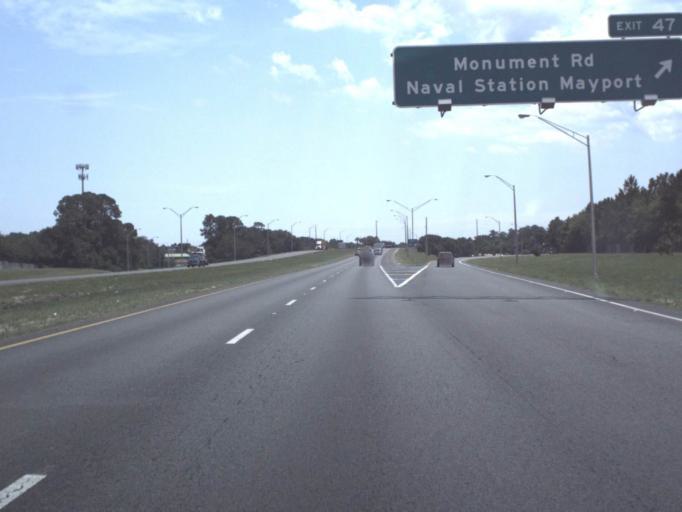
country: US
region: Florida
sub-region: Duval County
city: Jacksonville
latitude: 30.3443
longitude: -81.5462
